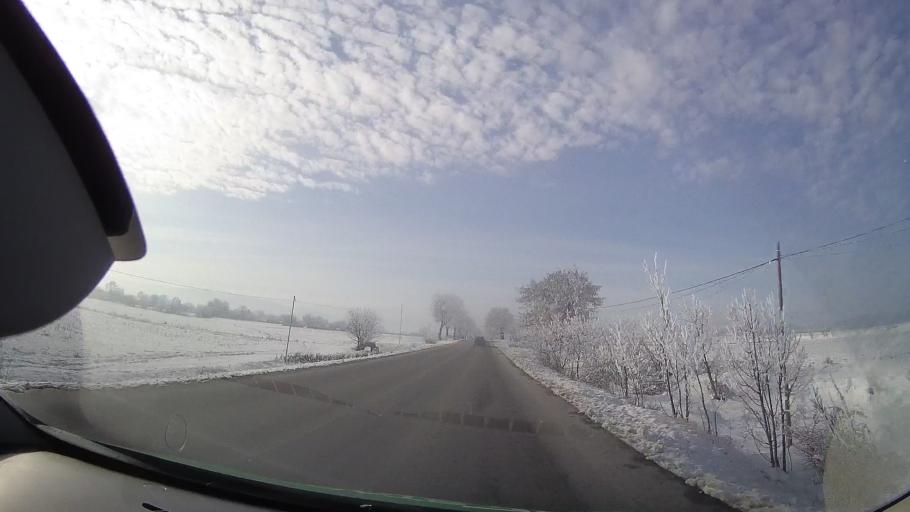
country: RO
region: Neamt
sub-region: Comuna Timisesti
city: Dumbrava
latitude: 47.2238
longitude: 26.4788
